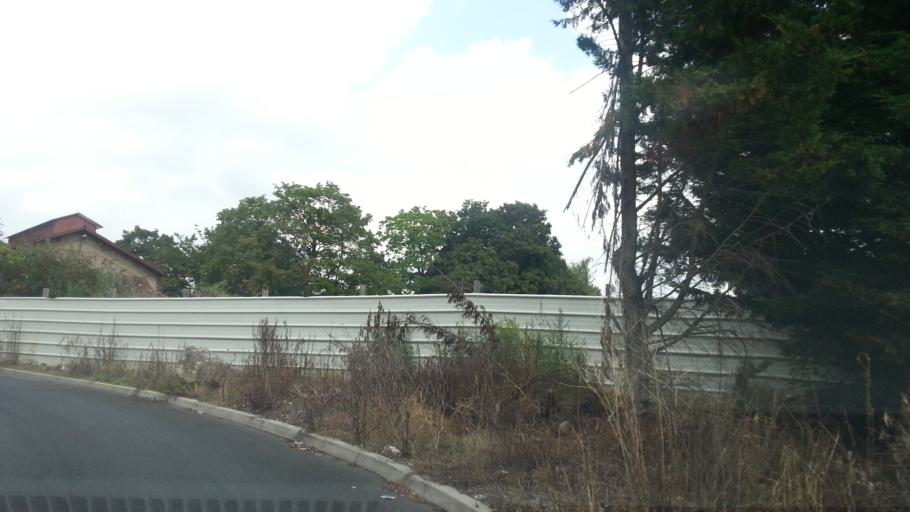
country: FR
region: Picardie
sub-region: Departement de l'Oise
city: Nogent-sur-Oise
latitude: 49.2588
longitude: 2.4621
